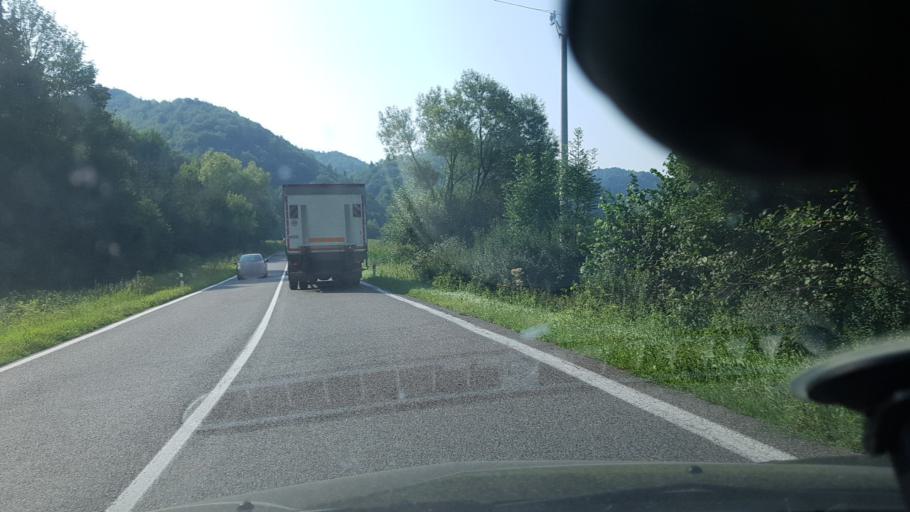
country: SK
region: Zilinsky
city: Tvrdosin
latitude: 49.2766
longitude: 19.4620
